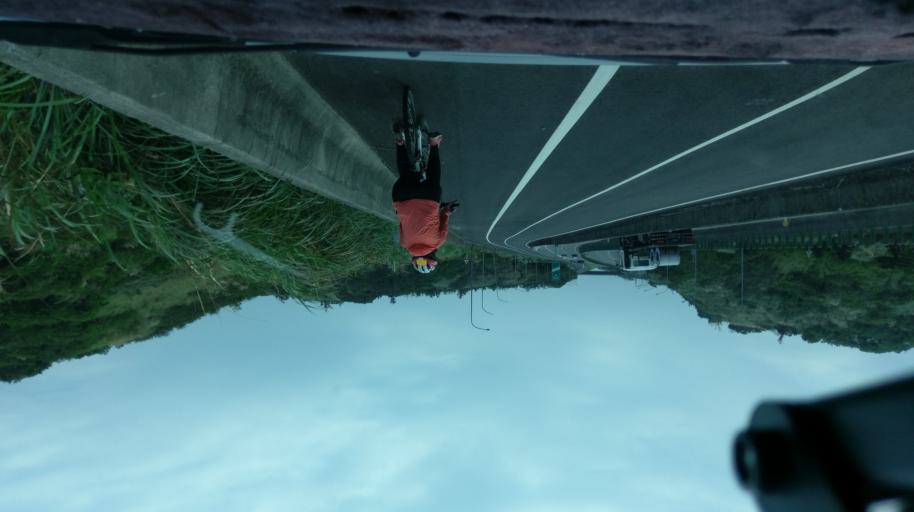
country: TW
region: Taiwan
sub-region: Miaoli
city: Miaoli
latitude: 24.5928
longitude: 120.7353
